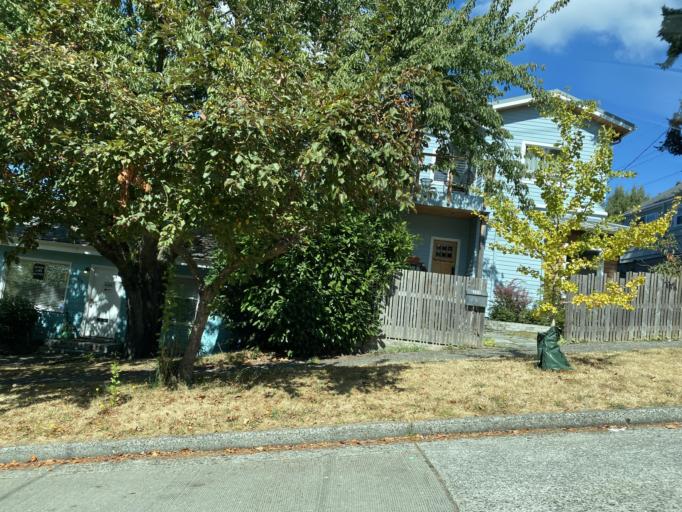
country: US
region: Washington
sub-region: King County
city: Seattle
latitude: 47.6622
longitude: -122.3613
